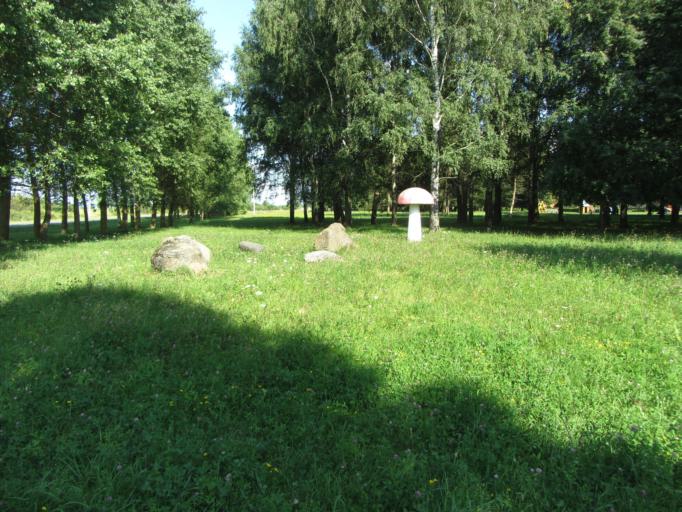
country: BY
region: Vitebsk
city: Vidzy
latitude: 55.3200
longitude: 26.6740
